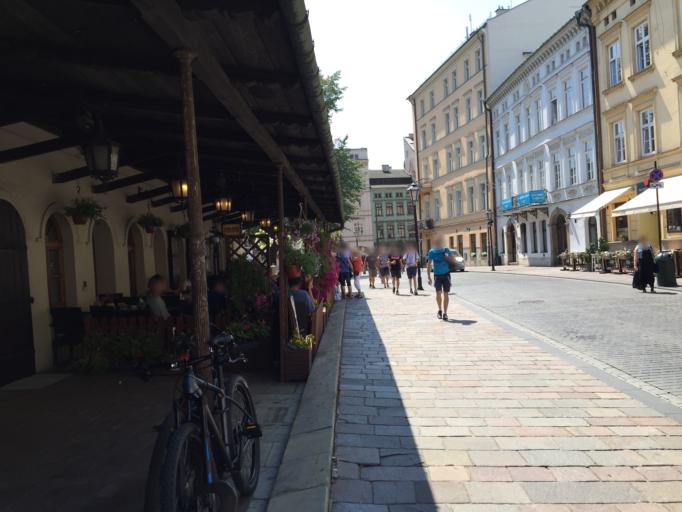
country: PL
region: Lesser Poland Voivodeship
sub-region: Krakow
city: Krakow
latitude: 50.0598
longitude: 19.9390
